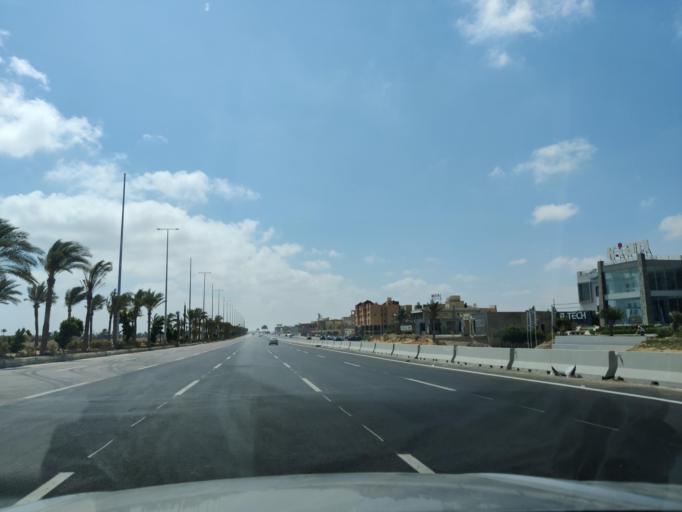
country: EG
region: Muhafazat Matruh
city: Al `Alamayn
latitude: 30.8329
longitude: 28.9642
